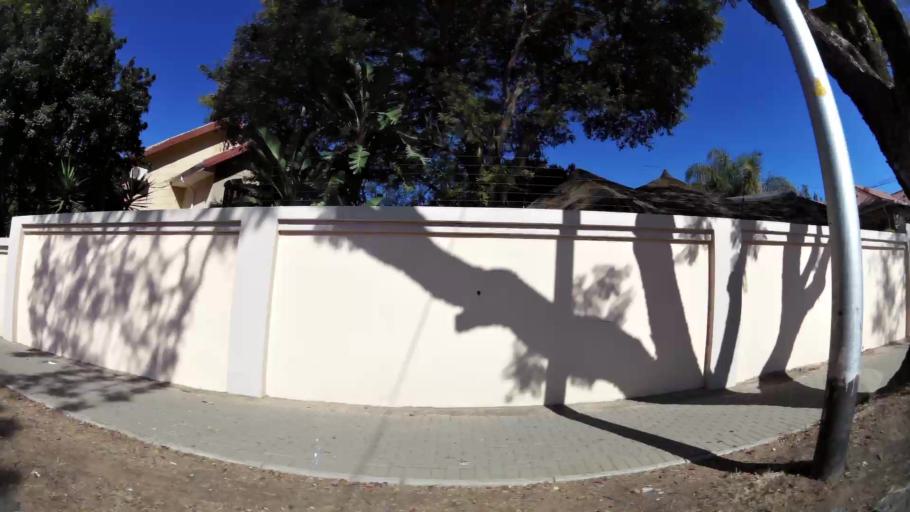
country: ZA
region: Gauteng
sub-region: City of Tshwane Metropolitan Municipality
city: Pretoria
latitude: -25.7579
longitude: 28.2181
